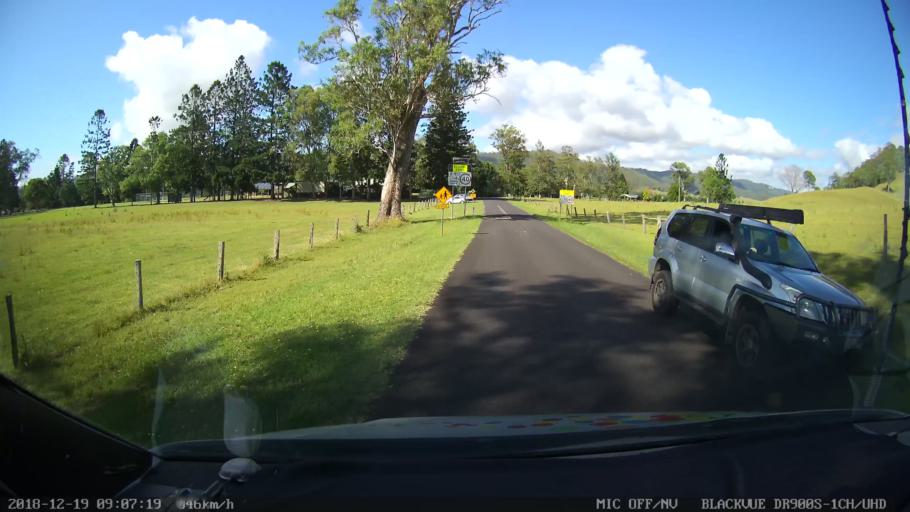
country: AU
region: New South Wales
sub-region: Kyogle
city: Kyogle
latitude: -28.4746
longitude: 152.9343
